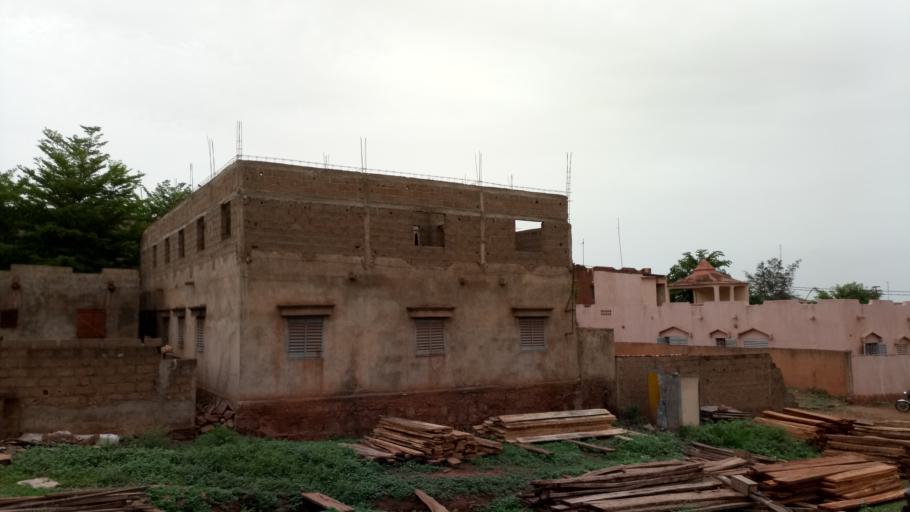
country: ML
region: Bamako
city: Bamako
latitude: 12.5882
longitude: -7.9955
